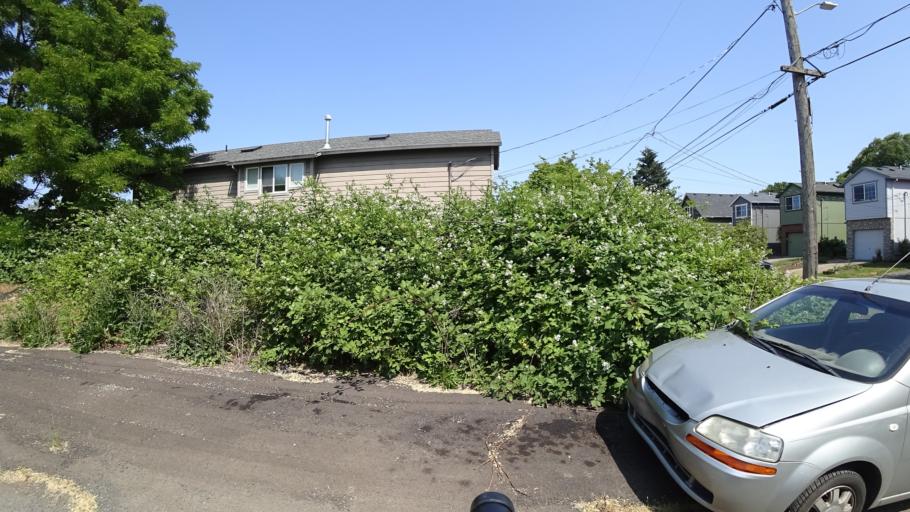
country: US
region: Oregon
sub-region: Multnomah County
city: Portland
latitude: 45.5786
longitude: -122.7013
